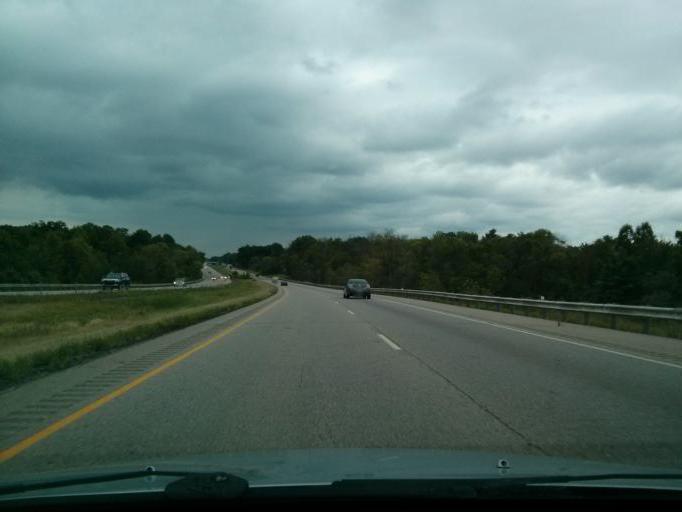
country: US
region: Ohio
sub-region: Mahoning County
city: Craig Beach
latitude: 41.1001
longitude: -81.0182
